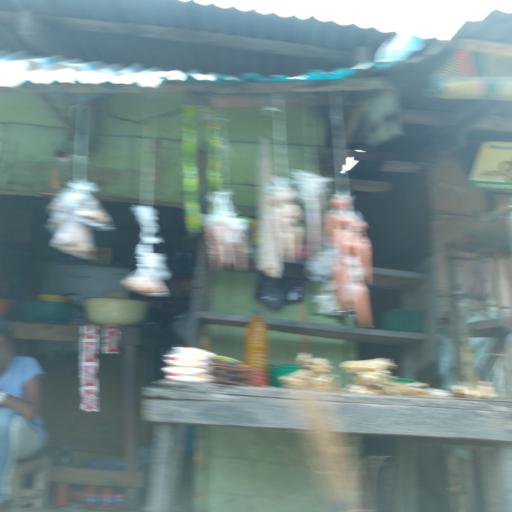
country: NG
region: Rivers
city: Port Harcourt
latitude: 4.7802
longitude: 7.0333
